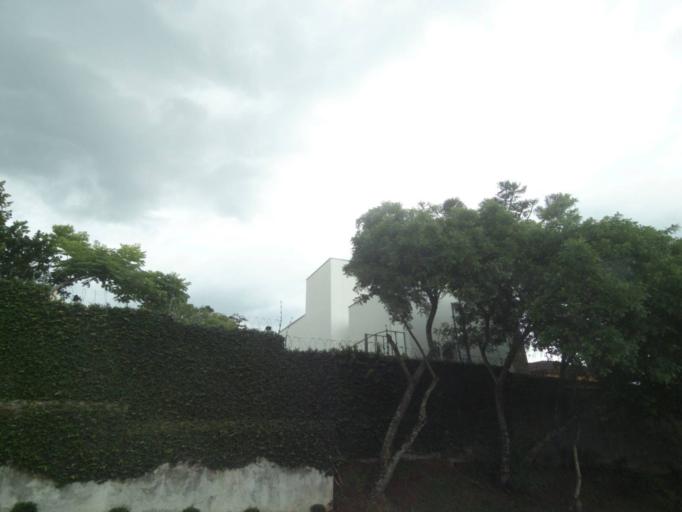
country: BR
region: Parana
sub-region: Curitiba
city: Curitiba
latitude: -25.4504
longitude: -49.3468
